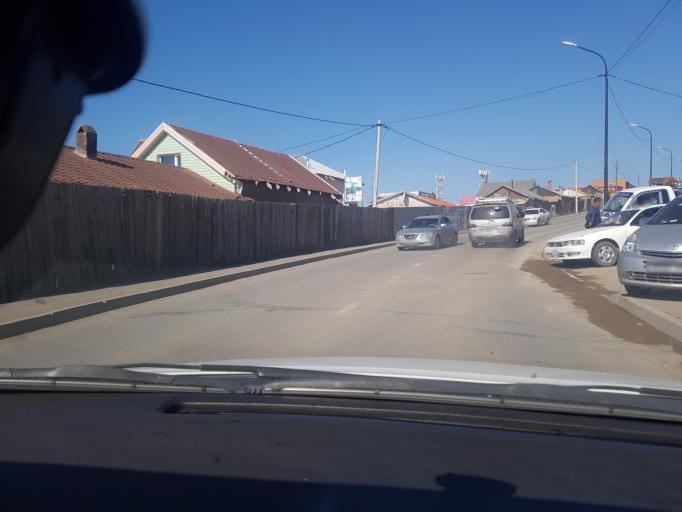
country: MN
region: Ulaanbaatar
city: Ulaanbaatar
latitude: 47.9494
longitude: 106.8652
